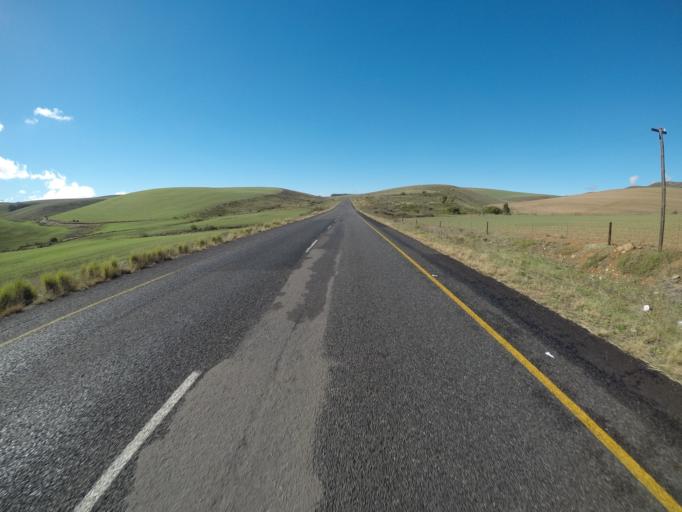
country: ZA
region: Western Cape
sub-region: Overberg District Municipality
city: Caledon
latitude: -34.1488
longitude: 19.4844
